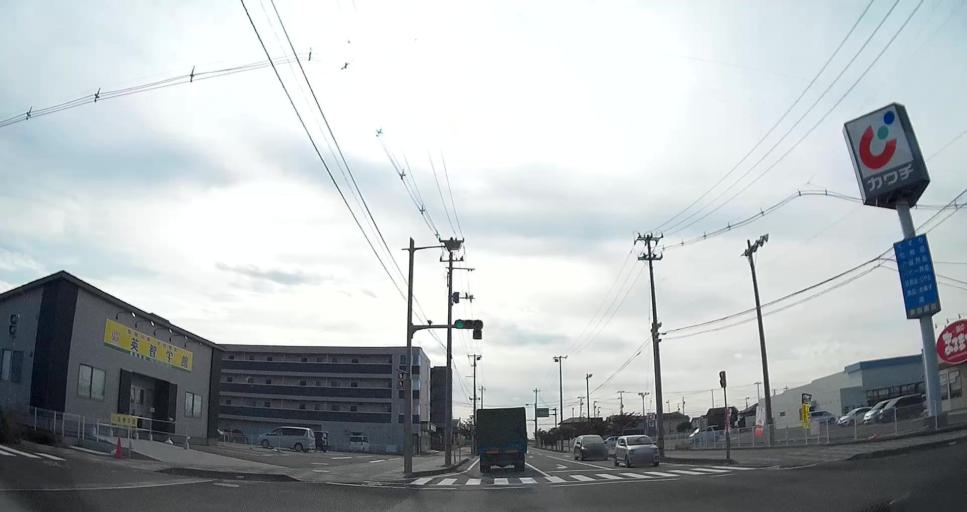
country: JP
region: Miyagi
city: Iwanuma
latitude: 38.1578
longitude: 140.9198
